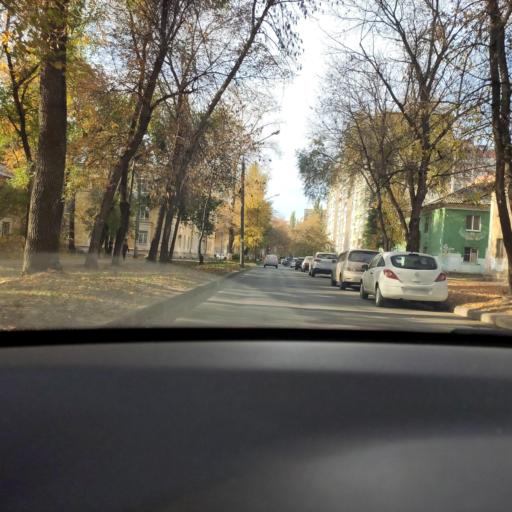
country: RU
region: Samara
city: Samara
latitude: 53.2170
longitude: 50.2482
